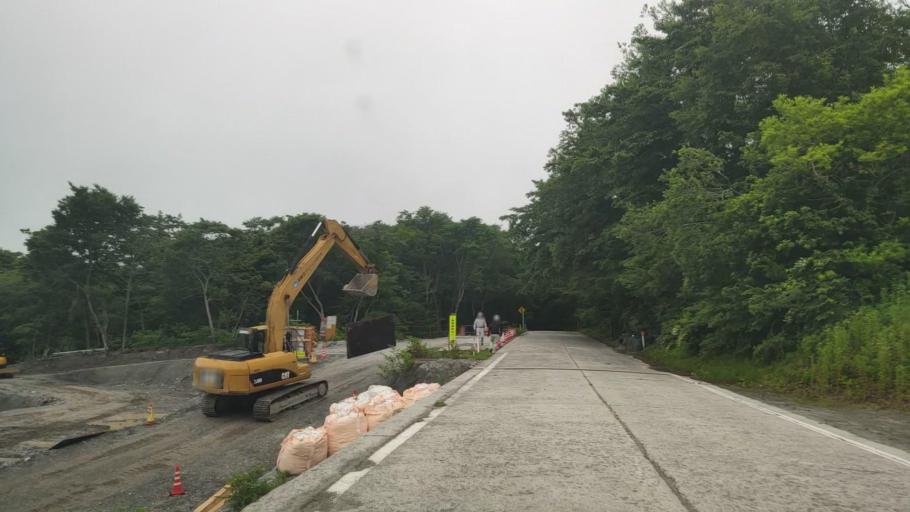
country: JP
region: Tottori
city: Yonago
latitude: 35.3553
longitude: 133.5373
